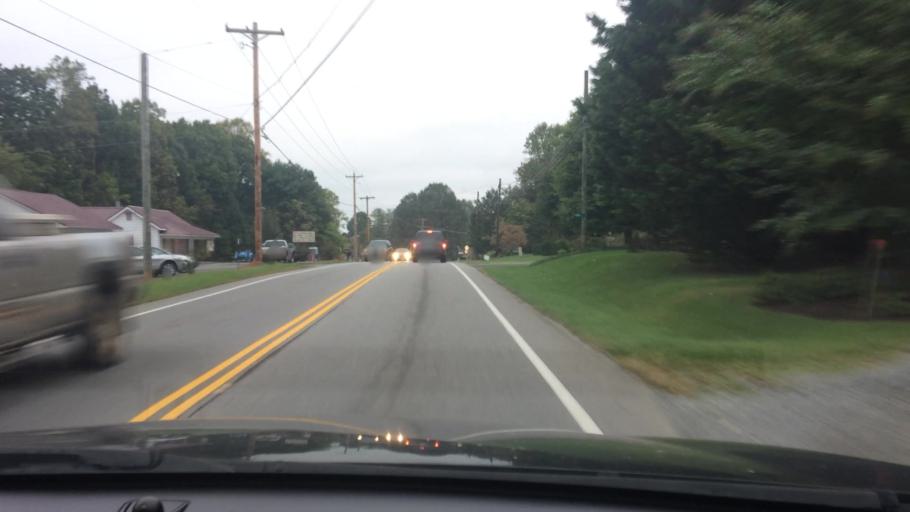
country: US
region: Virginia
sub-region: Franklin County
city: Henry Fork
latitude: 37.0194
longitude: -79.8146
